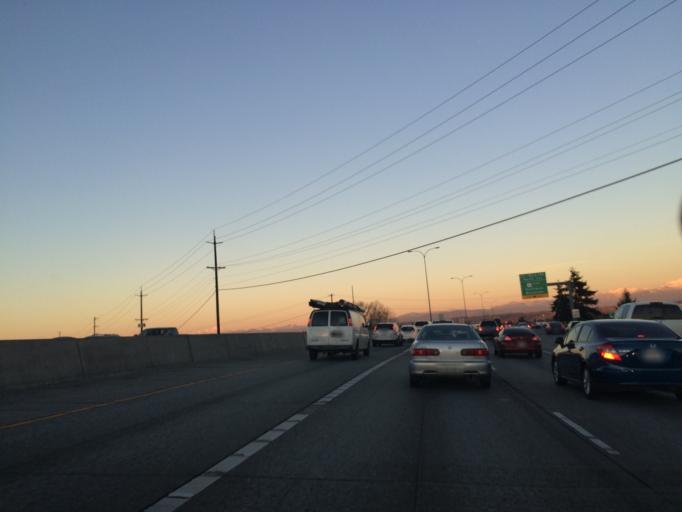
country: US
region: Washington
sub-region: Snohomish County
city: Everett
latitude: 47.9684
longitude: -122.1975
